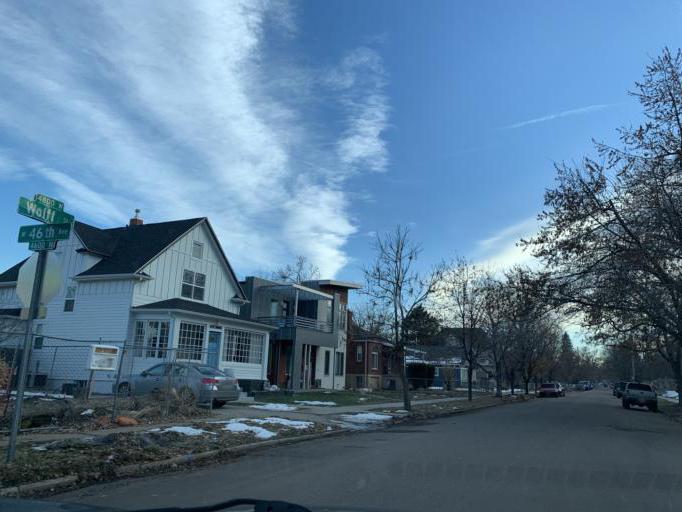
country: US
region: Colorado
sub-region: Jefferson County
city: Edgewater
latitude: 39.7801
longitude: -105.0487
